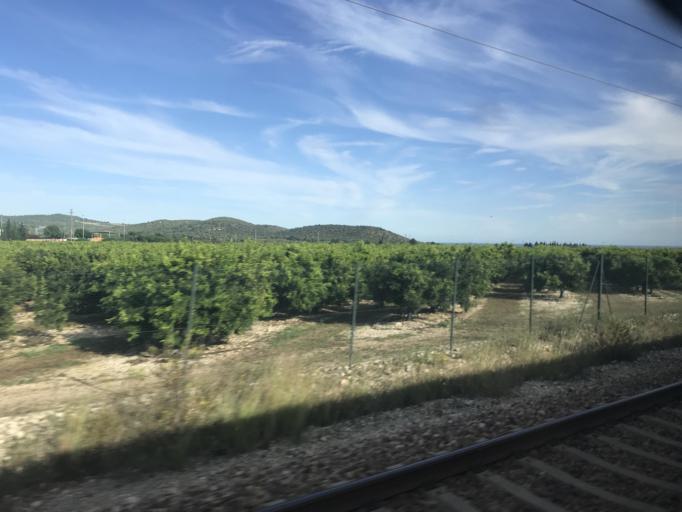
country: ES
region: Catalonia
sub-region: Provincia de Tarragona
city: Ulldecona
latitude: 40.5538
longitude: 0.4261
